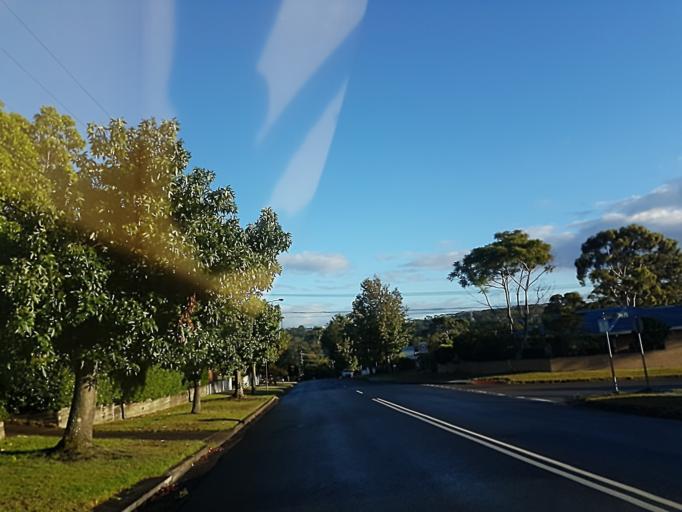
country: AU
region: New South Wales
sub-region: Warringah
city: Davidson
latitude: -33.7380
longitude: 151.2063
